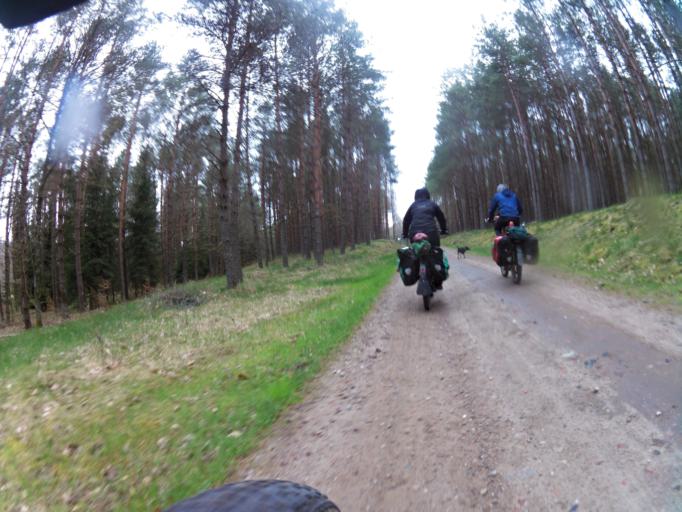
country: PL
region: West Pomeranian Voivodeship
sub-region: Powiat koszalinski
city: Bobolice
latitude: 54.0413
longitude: 16.6183
